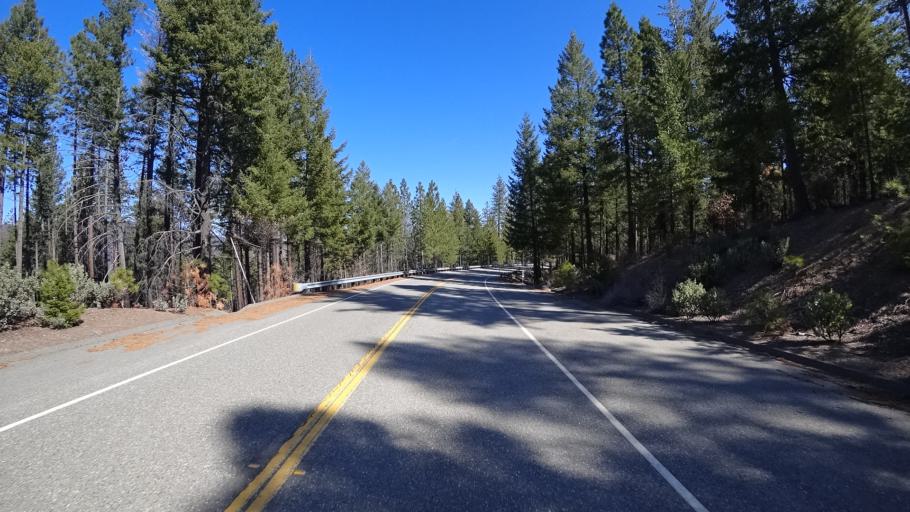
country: US
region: California
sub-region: Tehama County
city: Rancho Tehama Reserve
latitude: 39.6485
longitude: -122.7417
